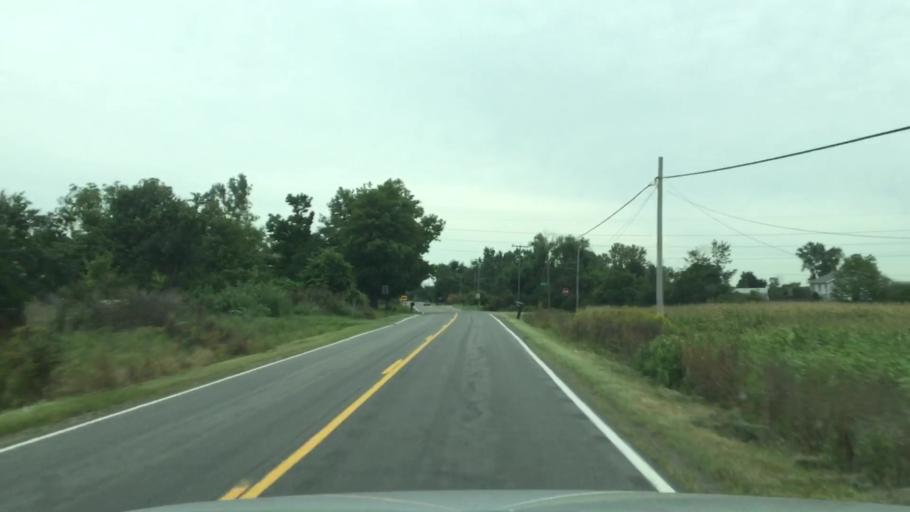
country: US
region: Michigan
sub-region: Washtenaw County
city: Milan
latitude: 42.1411
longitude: -83.6644
